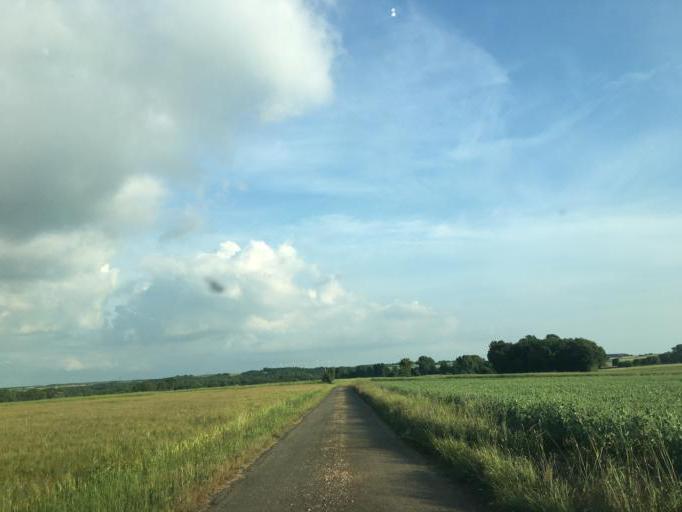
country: FR
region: Poitou-Charentes
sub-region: Departement de la Charente-Maritime
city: Saint-Jean-d'Angely
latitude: 46.0719
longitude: -0.5765
